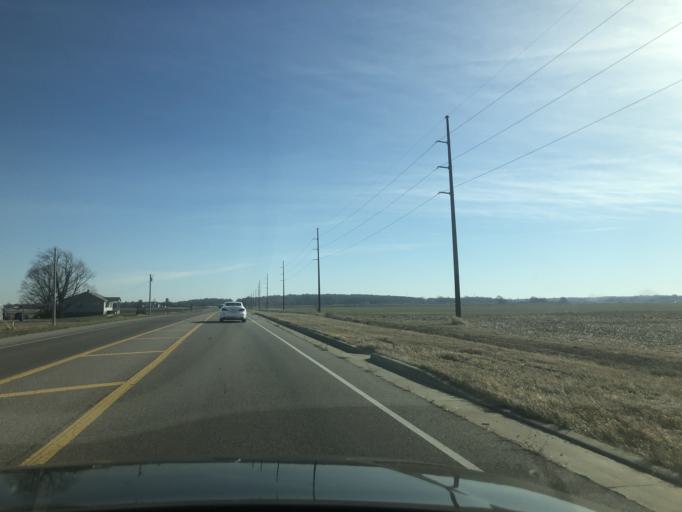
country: US
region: Indiana
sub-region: Warrick County
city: Newburgh
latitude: 37.9912
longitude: -87.4382
